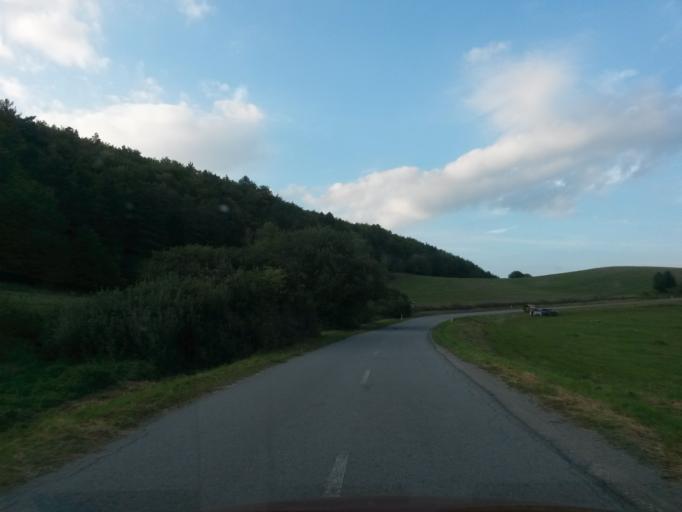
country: SK
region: Kosicky
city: Gelnica
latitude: 48.9337
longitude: 21.0454
